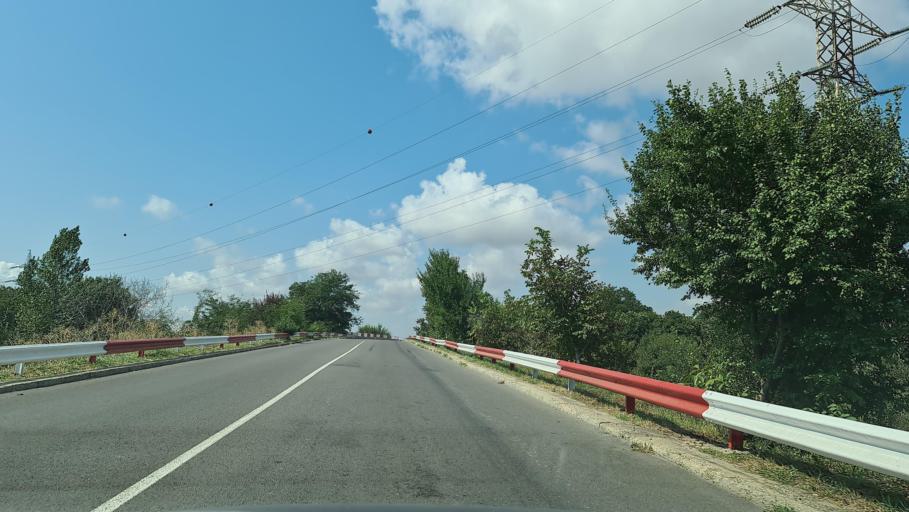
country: RO
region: Constanta
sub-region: Oras Eforie
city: Eforie Nord
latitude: 44.0759
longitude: 28.6277
